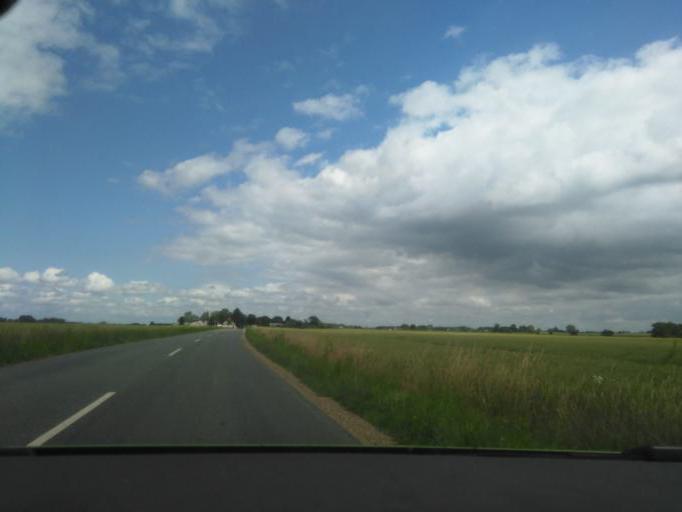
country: DK
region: Zealand
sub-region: Kalundborg Kommune
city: Gorlev
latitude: 55.5453
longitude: 11.1738
